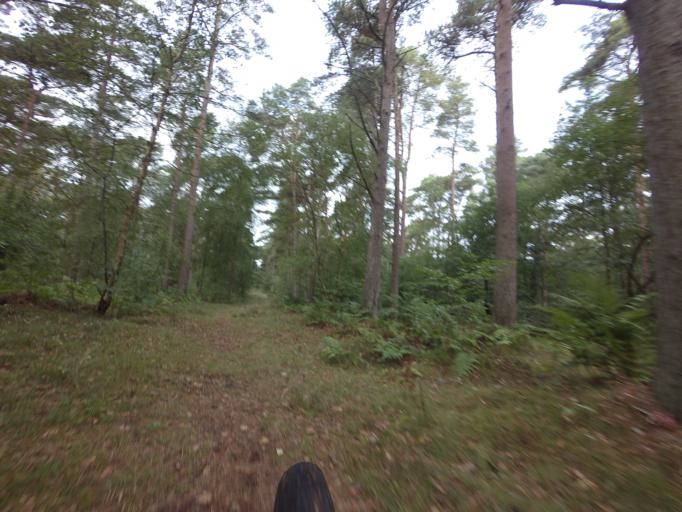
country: DK
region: North Denmark
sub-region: Hjorring Kommune
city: Hirtshals
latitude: 57.5790
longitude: 10.0516
